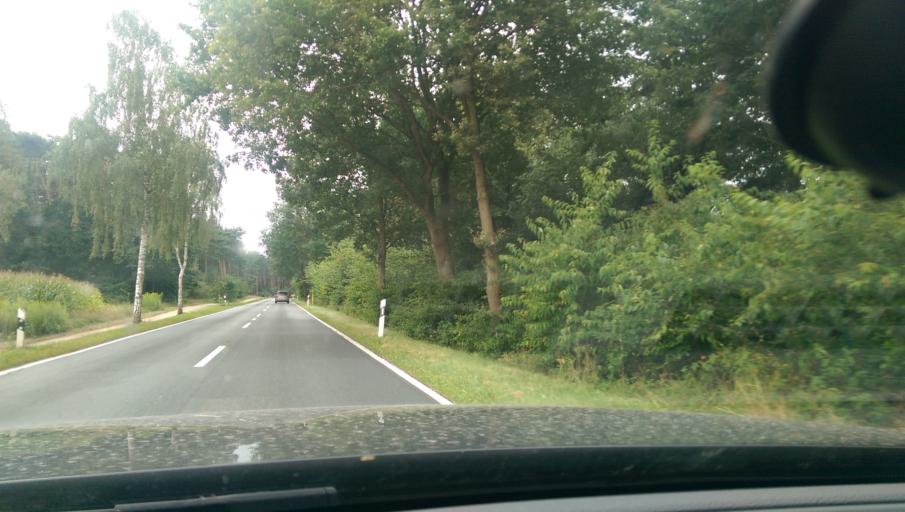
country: DE
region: Lower Saxony
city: Linsburg
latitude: 52.5210
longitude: 9.3290
